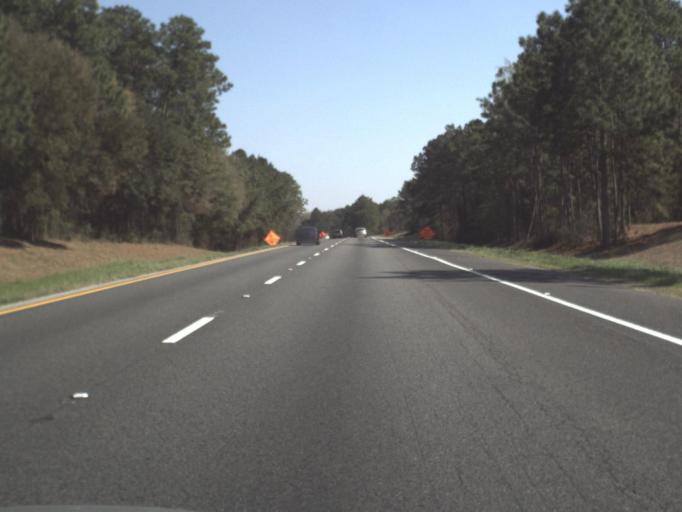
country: US
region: Florida
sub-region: Jackson County
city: Sneads
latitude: 30.6534
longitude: -85.0317
